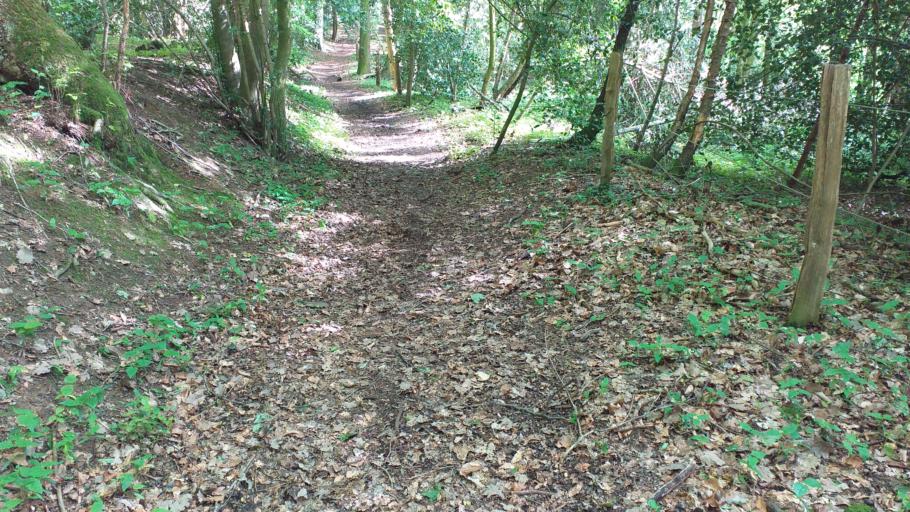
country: BE
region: Wallonia
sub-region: Province de Liege
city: La Calamine
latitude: 50.7247
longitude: 6.0500
